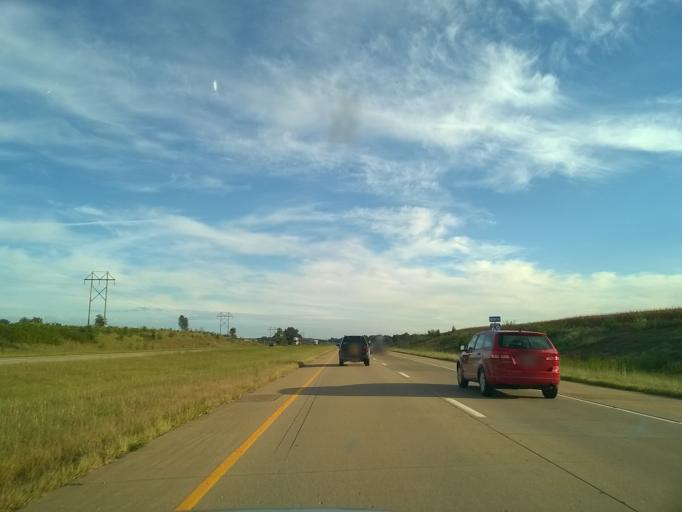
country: US
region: Indiana
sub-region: Vanderburgh County
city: Melody Hill
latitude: 38.0981
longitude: -87.4763
